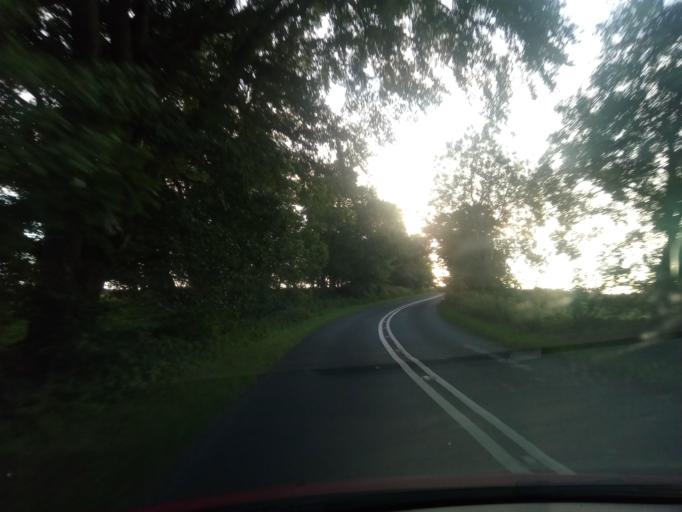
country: GB
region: England
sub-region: Northumberland
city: Bardon Mill
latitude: 54.8061
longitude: -2.3792
